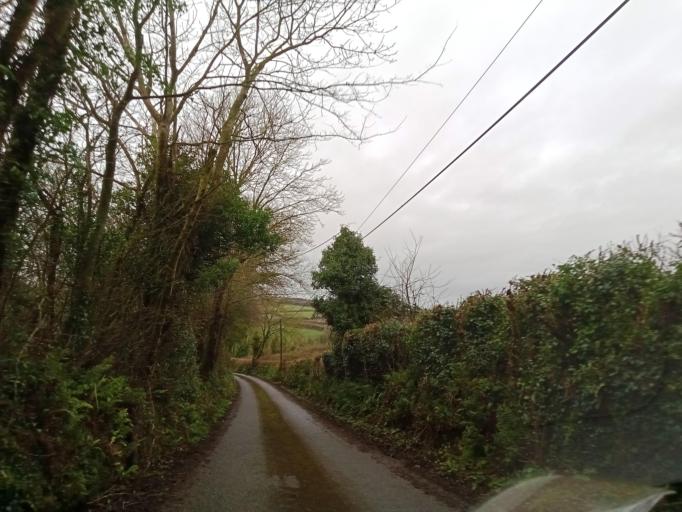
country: IE
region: Munster
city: Fethard
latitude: 52.5611
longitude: -7.7129
